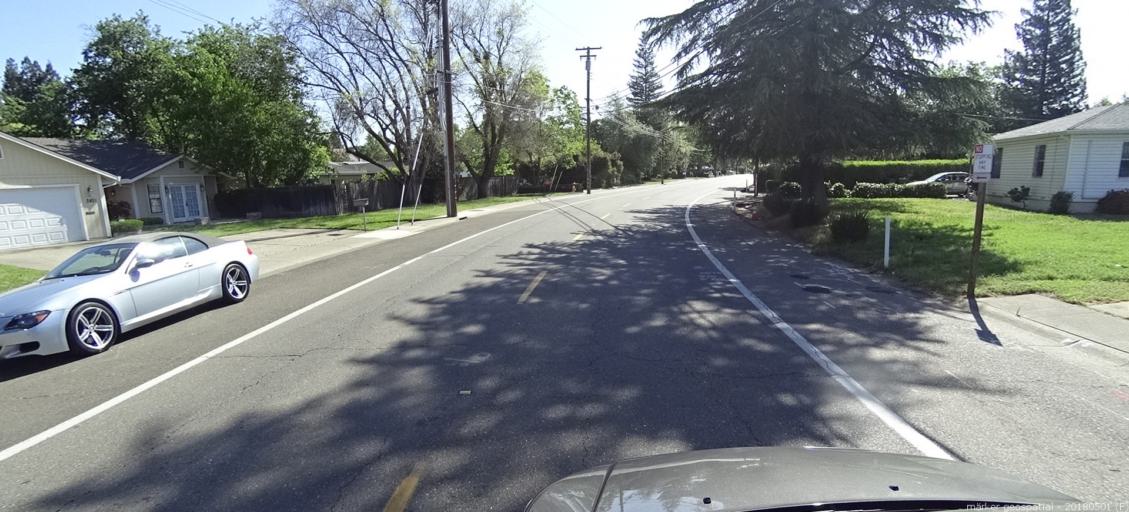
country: US
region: California
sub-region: Sacramento County
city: Arden-Arcade
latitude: 38.6344
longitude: -121.3760
